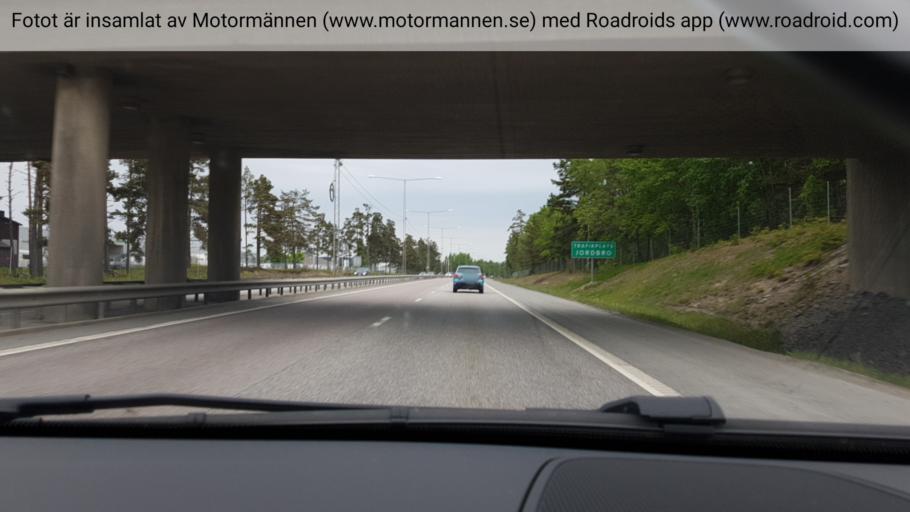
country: SE
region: Stockholm
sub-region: Haninge Kommun
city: Haninge
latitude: 59.1683
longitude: 18.1589
